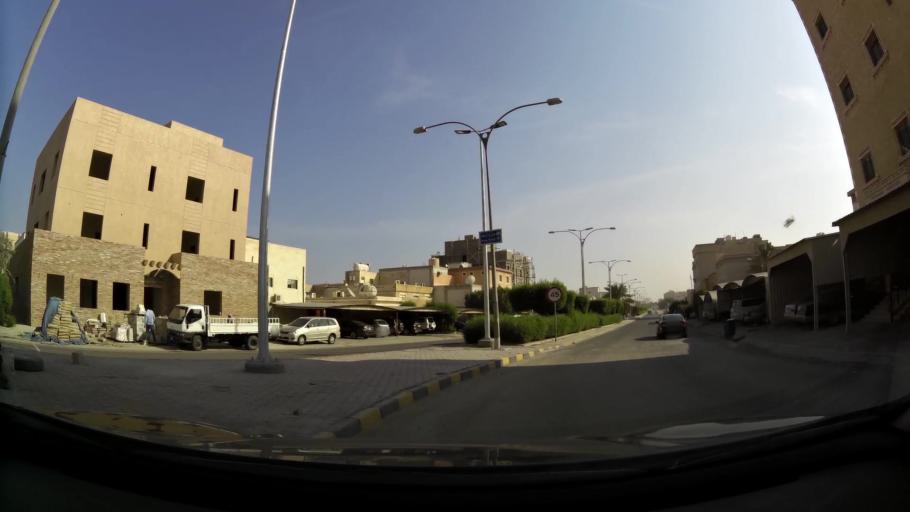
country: KW
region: Al Ahmadi
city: Ar Riqqah
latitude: 29.1501
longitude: 48.1054
